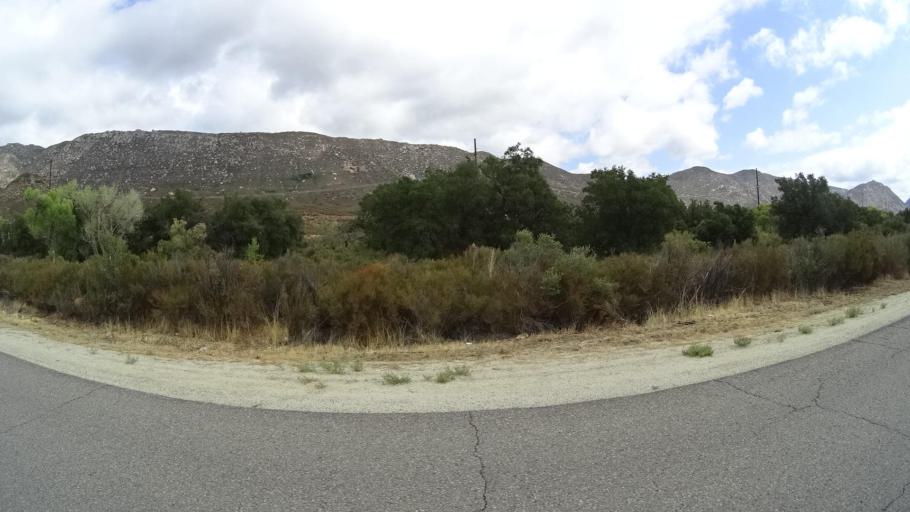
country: US
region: California
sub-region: San Diego County
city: Pine Valley
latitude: 32.7678
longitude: -116.4928
